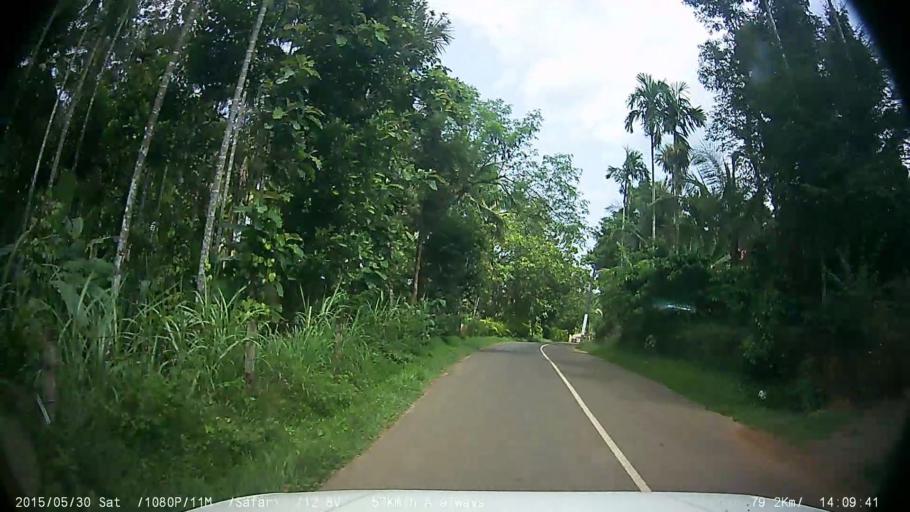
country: IN
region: Kerala
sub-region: Wayanad
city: Panamaram
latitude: 11.8046
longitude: 76.0511
